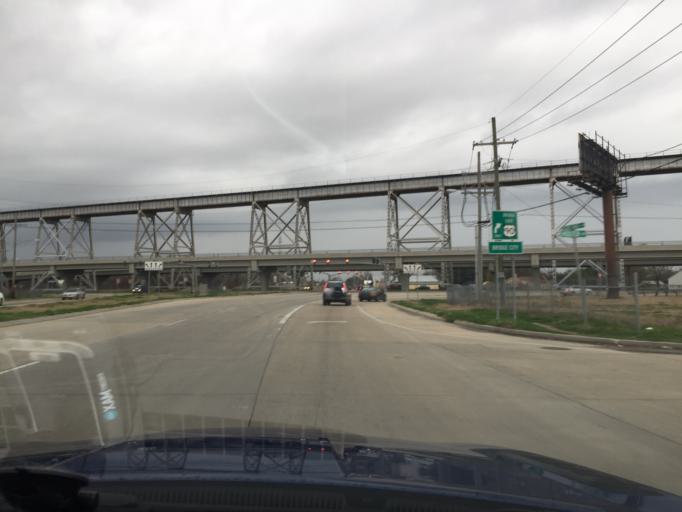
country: US
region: Louisiana
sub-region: Jefferson Parish
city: Bridge City
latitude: 29.9301
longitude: -90.1638
